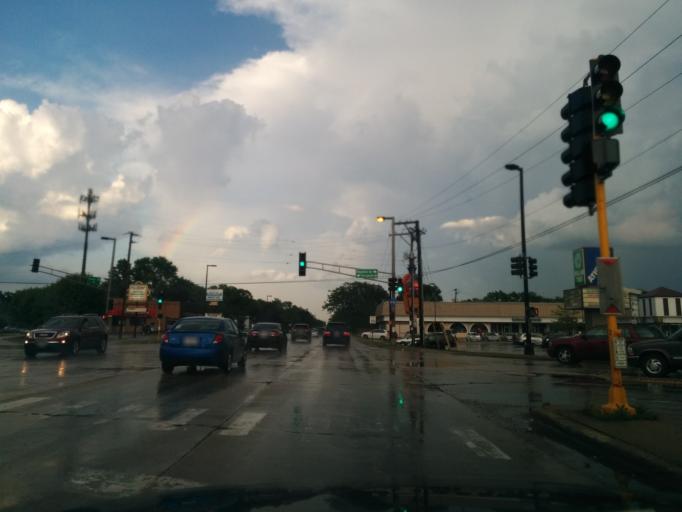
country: US
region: Illinois
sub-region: Cook County
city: Burbank
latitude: 41.7338
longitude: -87.7803
